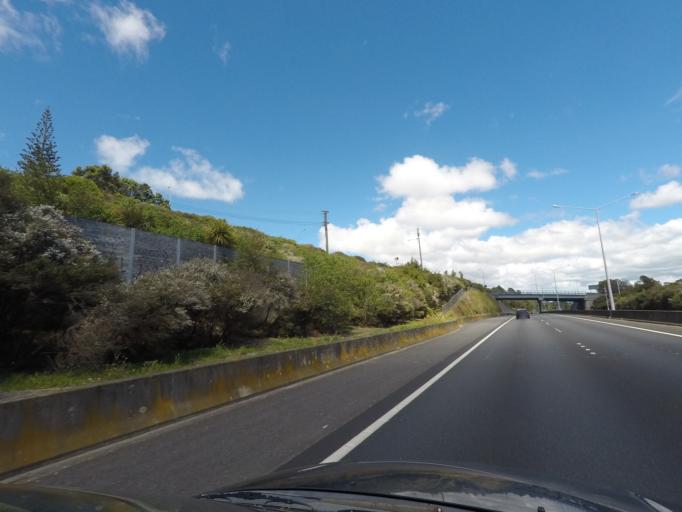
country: NZ
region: Auckland
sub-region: Auckland
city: North Shore
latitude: -36.7800
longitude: 174.6792
